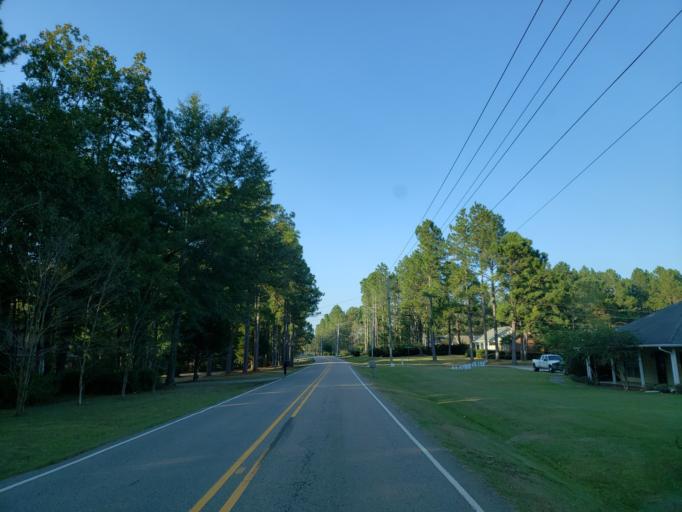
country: US
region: Mississippi
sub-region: Lamar County
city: West Hattiesburg
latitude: 31.3003
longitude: -89.4459
